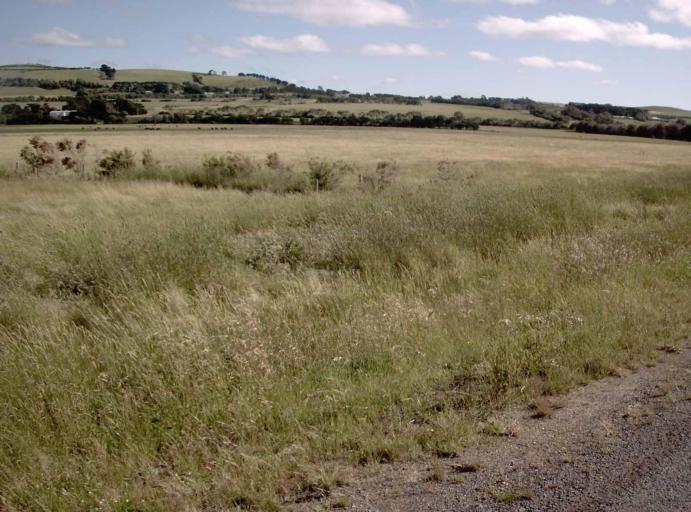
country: AU
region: Victoria
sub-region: Bass Coast
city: North Wonthaggi
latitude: -38.5058
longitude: 145.4542
